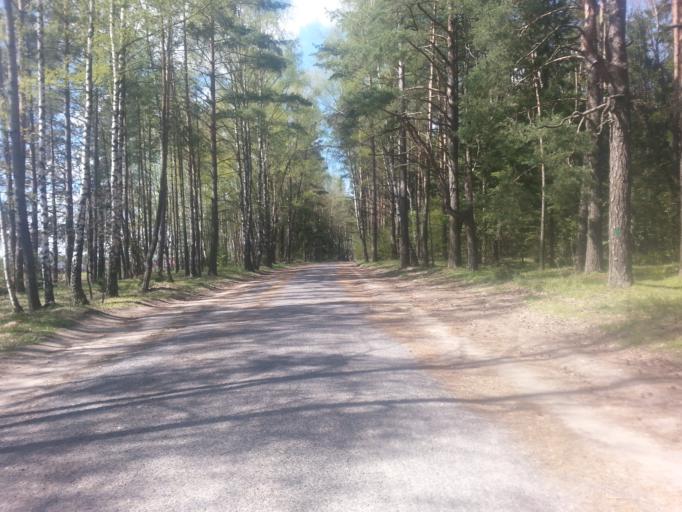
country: BY
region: Minsk
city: Narach
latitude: 54.9202
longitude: 26.6958
